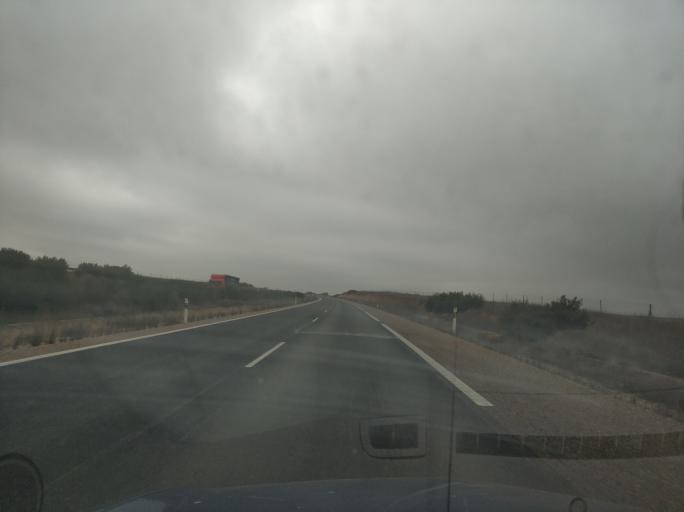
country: ES
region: Castille and Leon
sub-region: Provincia de Zamora
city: Canizal
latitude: 41.1930
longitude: -5.3525
